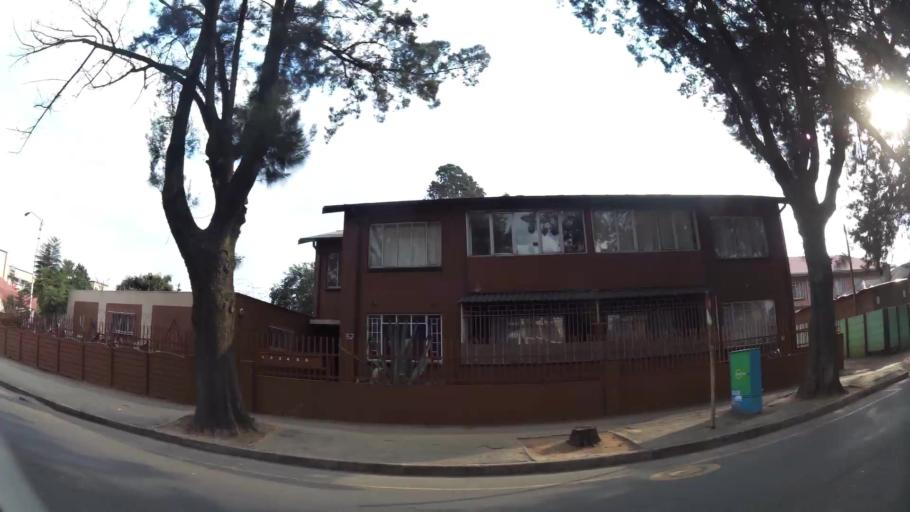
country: ZA
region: Gauteng
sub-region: Ekurhuleni Metropolitan Municipality
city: Germiston
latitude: -26.2239
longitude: 28.1697
